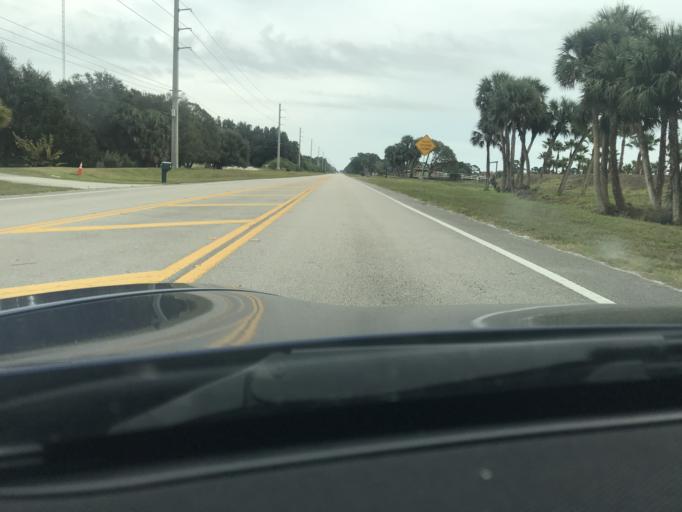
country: US
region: Florida
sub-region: Indian River County
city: Winter Beach
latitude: 27.7339
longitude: -80.4609
